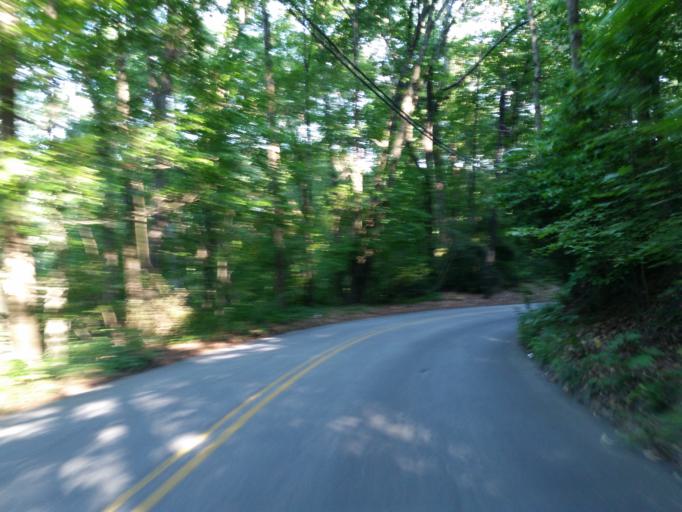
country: US
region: Georgia
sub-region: Cobb County
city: Vinings
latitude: 33.8627
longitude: -84.4251
